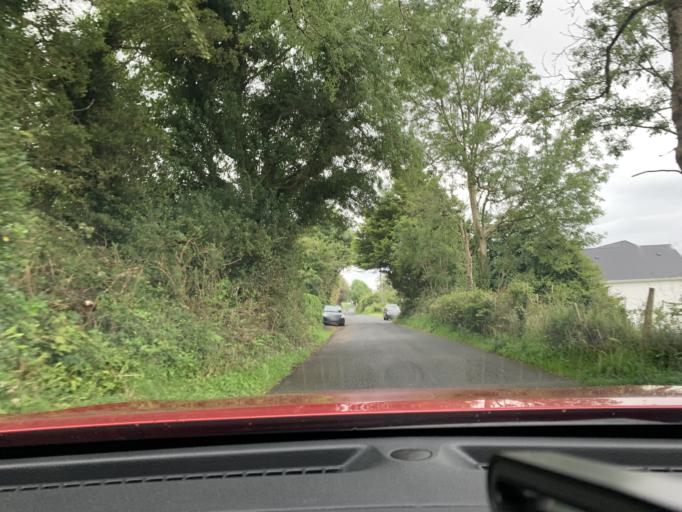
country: IE
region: Connaught
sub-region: County Leitrim
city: Manorhamilton
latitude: 54.3091
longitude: -8.1877
